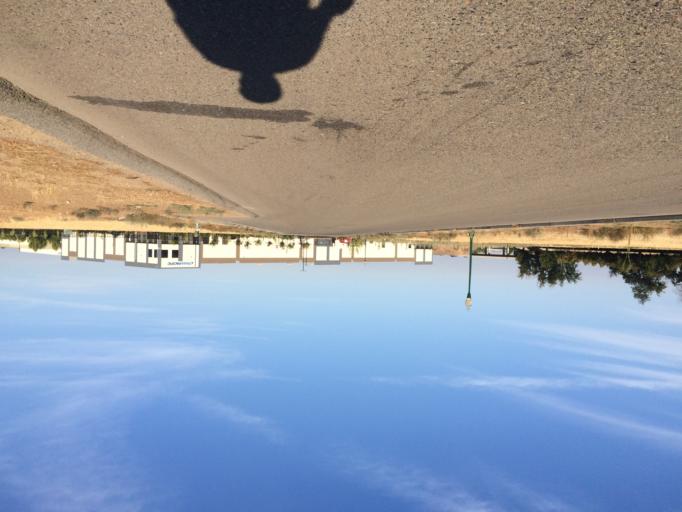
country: US
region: California
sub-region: Fresno County
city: Sunnyside
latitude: 36.7490
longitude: -119.6804
